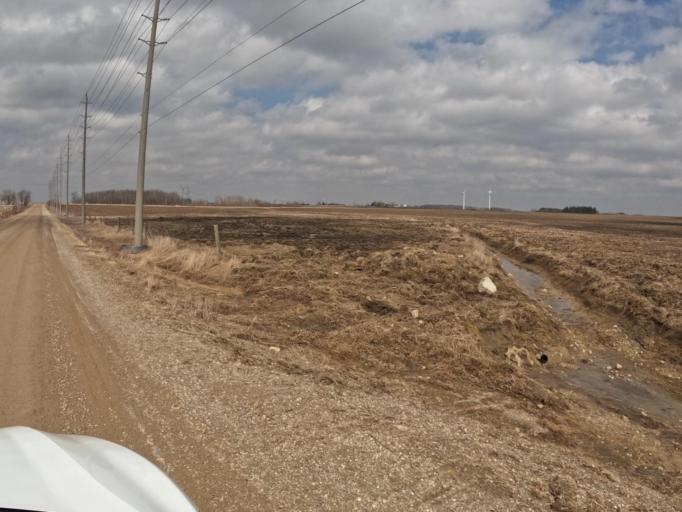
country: CA
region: Ontario
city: Shelburne
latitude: 44.0505
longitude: -80.3200
